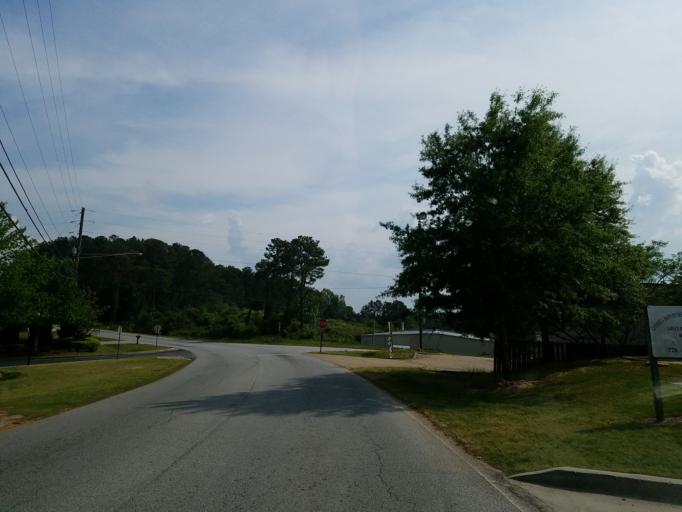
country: US
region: Georgia
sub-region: Paulding County
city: Dallas
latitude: 33.9075
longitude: -84.8033
